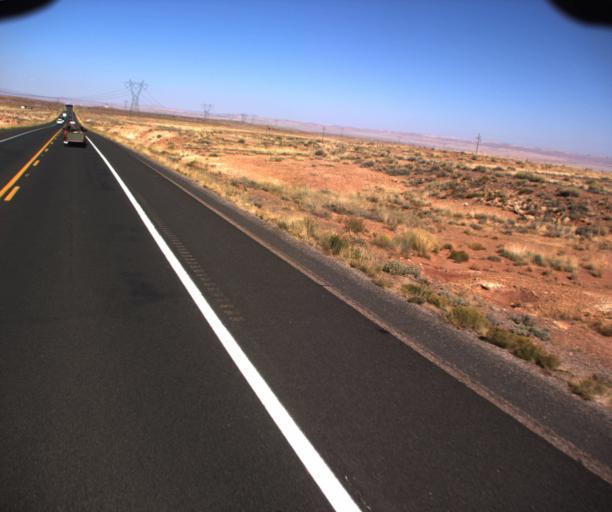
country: US
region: Arizona
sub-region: Coconino County
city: Tuba City
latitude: 35.8138
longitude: -111.4425
